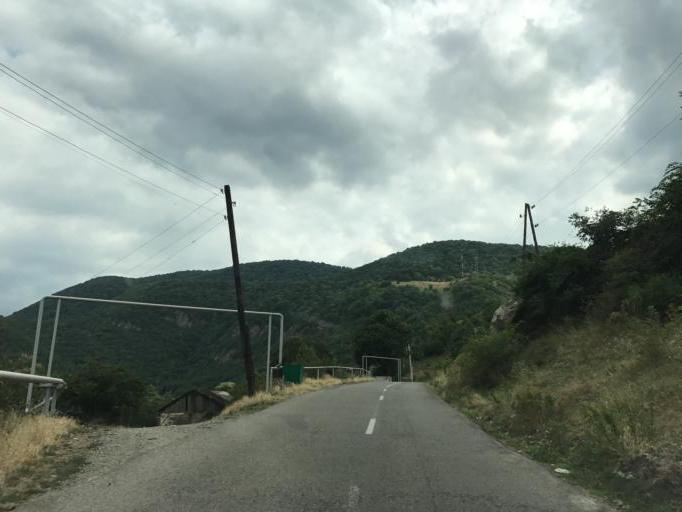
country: AM
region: Tavush
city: Haghartsin
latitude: 40.7443
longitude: 45.0243
